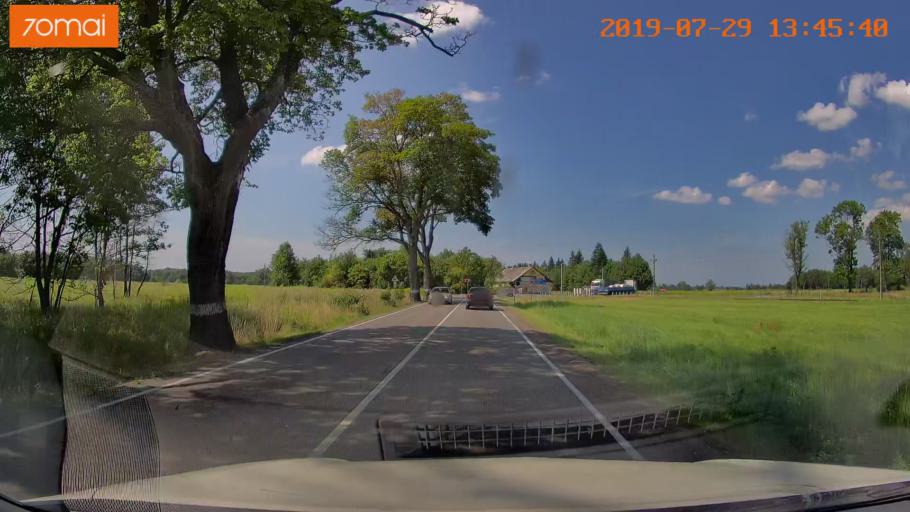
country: RU
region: Kaliningrad
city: Primorsk
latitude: 54.7398
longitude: 20.0706
